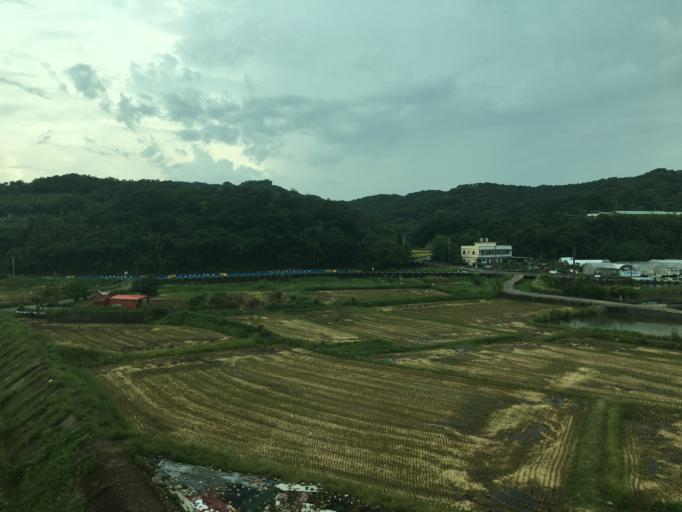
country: TW
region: Taiwan
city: Taoyuan City
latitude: 25.0805
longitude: 121.3006
